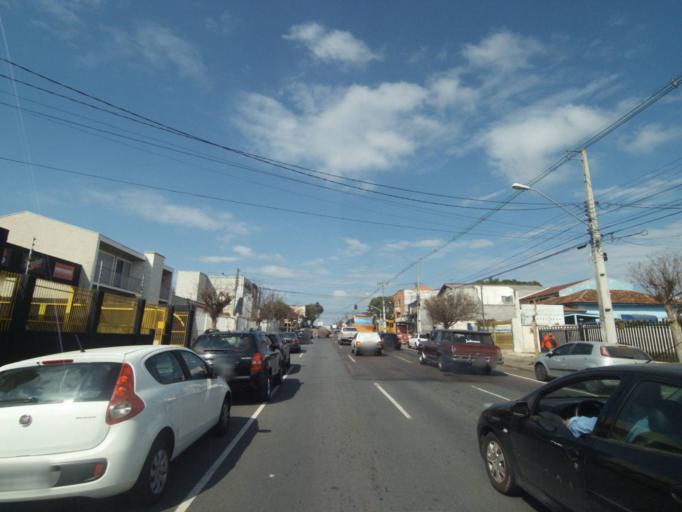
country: BR
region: Parana
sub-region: Curitiba
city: Curitiba
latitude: -25.4534
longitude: -49.2664
